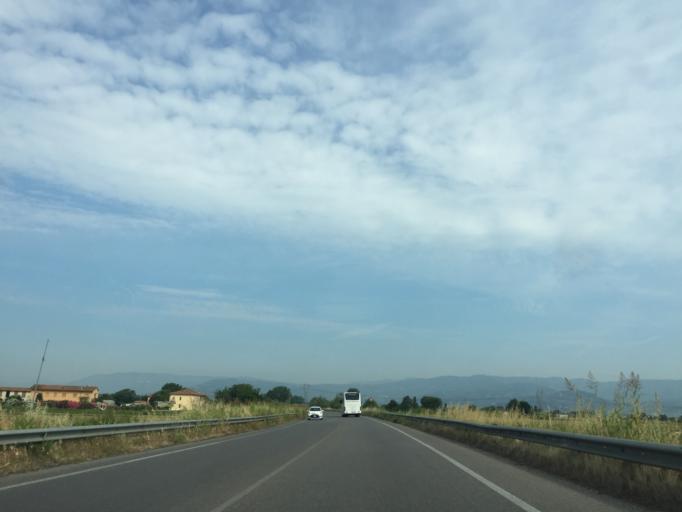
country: IT
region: Tuscany
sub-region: Provincia di Pistoia
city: Cintolese
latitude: 43.8432
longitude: 10.8173
